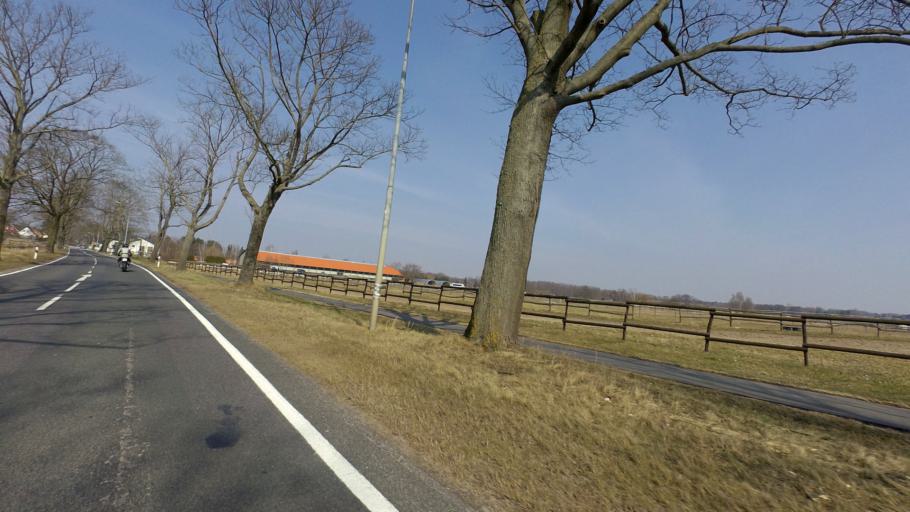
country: DE
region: Brandenburg
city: Werder
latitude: 52.4188
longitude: 12.8949
